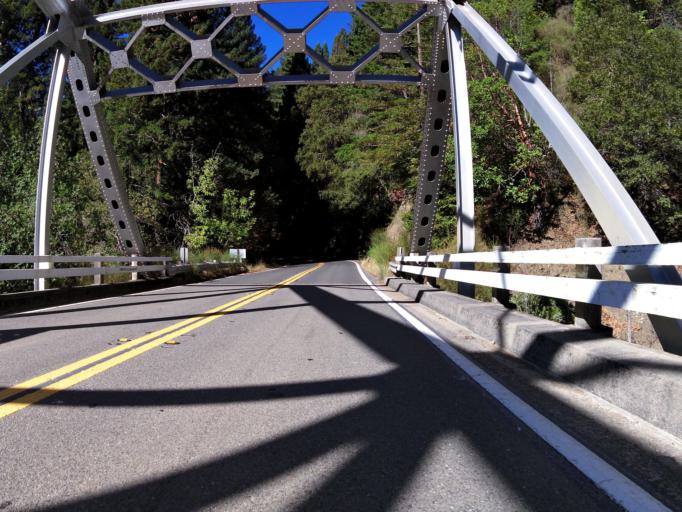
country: US
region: California
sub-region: Humboldt County
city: Redway
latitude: 39.8641
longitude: -123.7227
